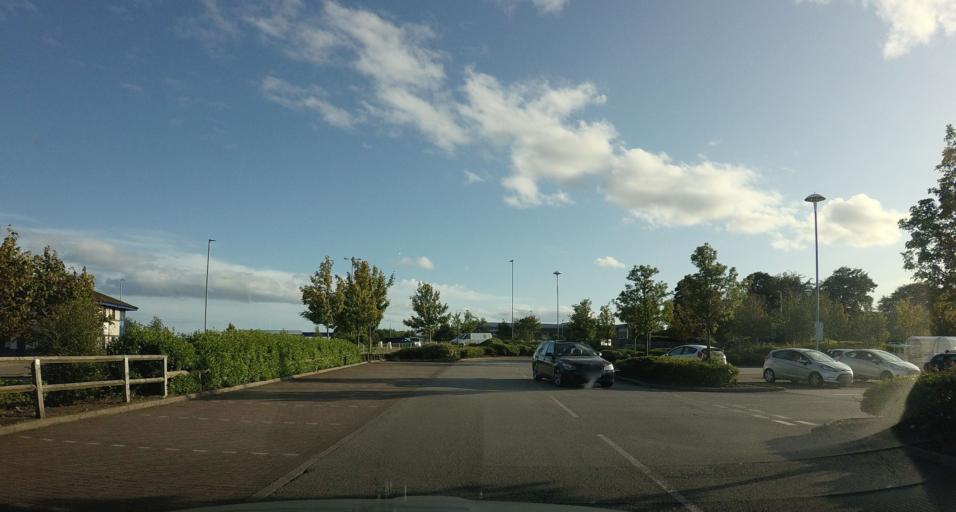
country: GB
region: Scotland
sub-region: Aberdeenshire
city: Westhill
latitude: 57.1492
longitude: -2.2740
